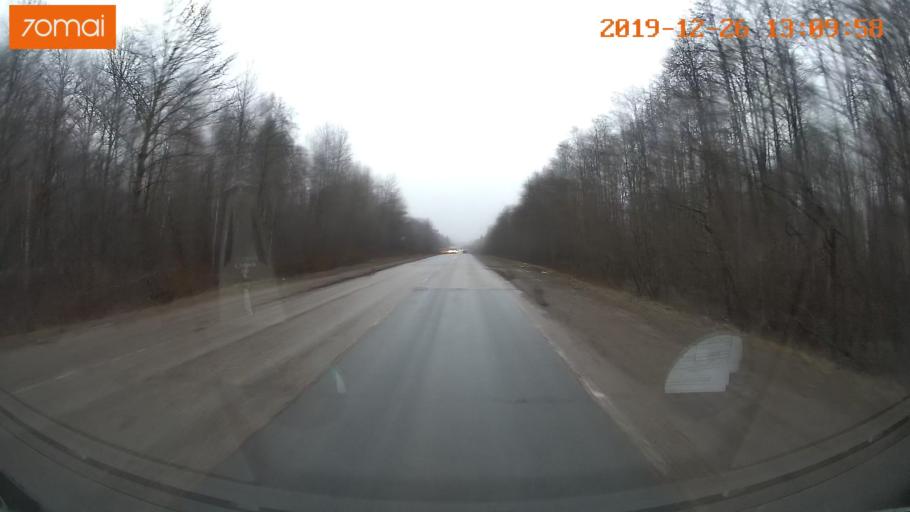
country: RU
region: Vologda
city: Cherepovets
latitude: 59.0408
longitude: 37.9692
